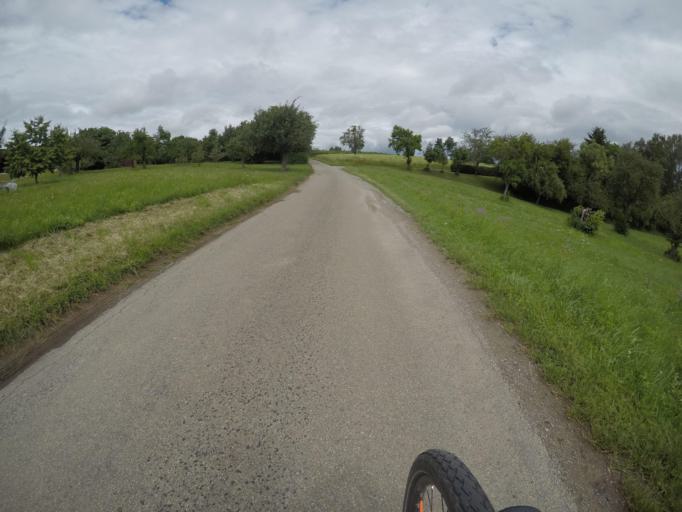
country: DE
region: Baden-Wuerttemberg
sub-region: Regierungsbezirk Stuttgart
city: Gartringen
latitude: 48.6467
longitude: 8.8829
